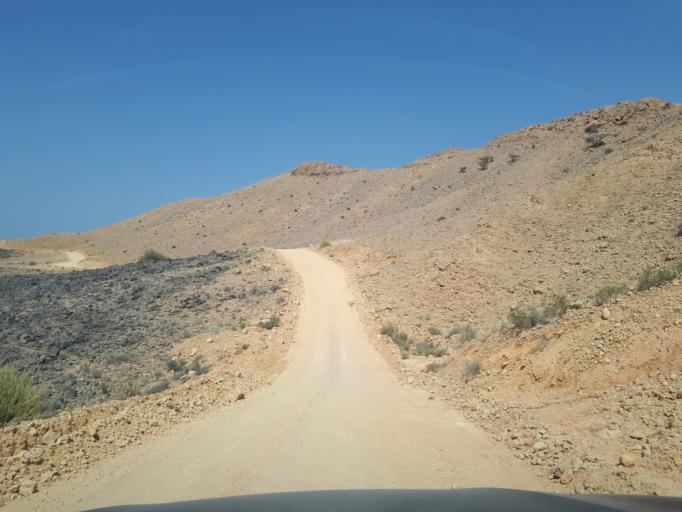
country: OM
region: Ash Sharqiyah
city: Ibra'
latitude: 23.0858
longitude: 58.9445
